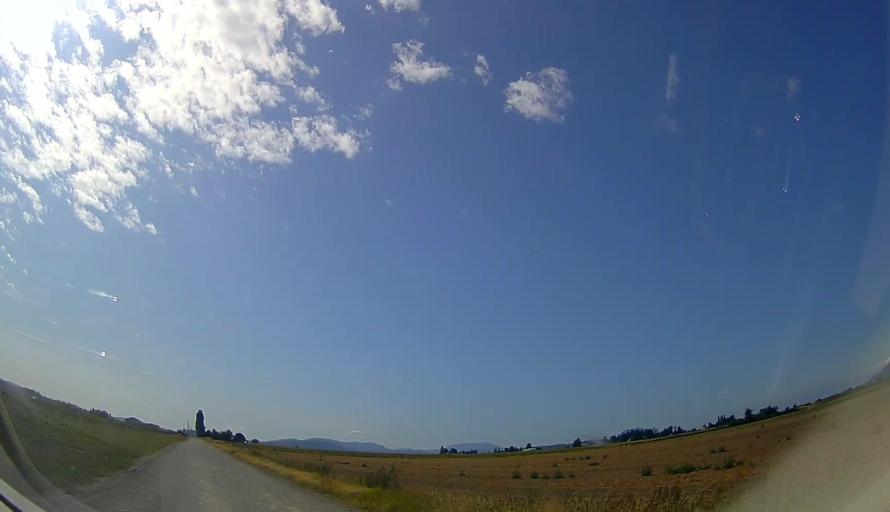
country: US
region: Washington
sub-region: Skagit County
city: Burlington
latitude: 48.5234
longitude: -122.4343
